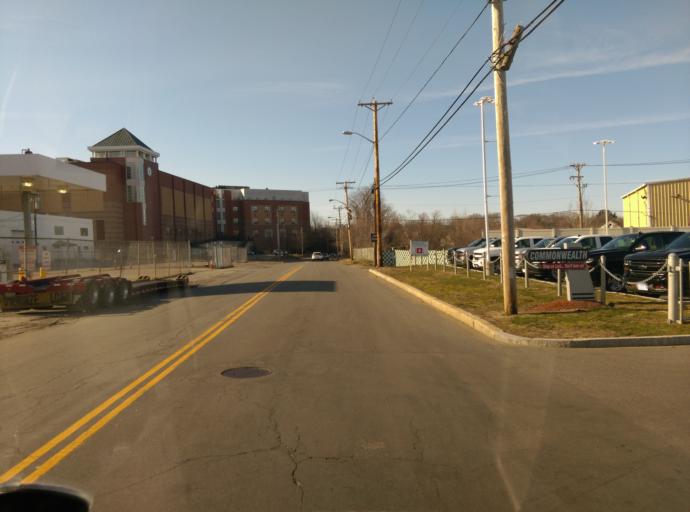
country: US
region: Massachusetts
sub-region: Essex County
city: North Andover
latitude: 42.7174
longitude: -71.1416
